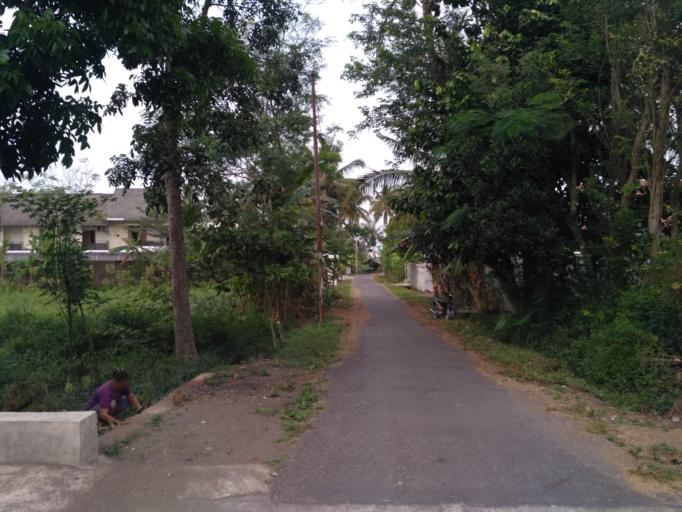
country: ID
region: Daerah Istimewa Yogyakarta
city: Melati
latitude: -7.7058
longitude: 110.4080
